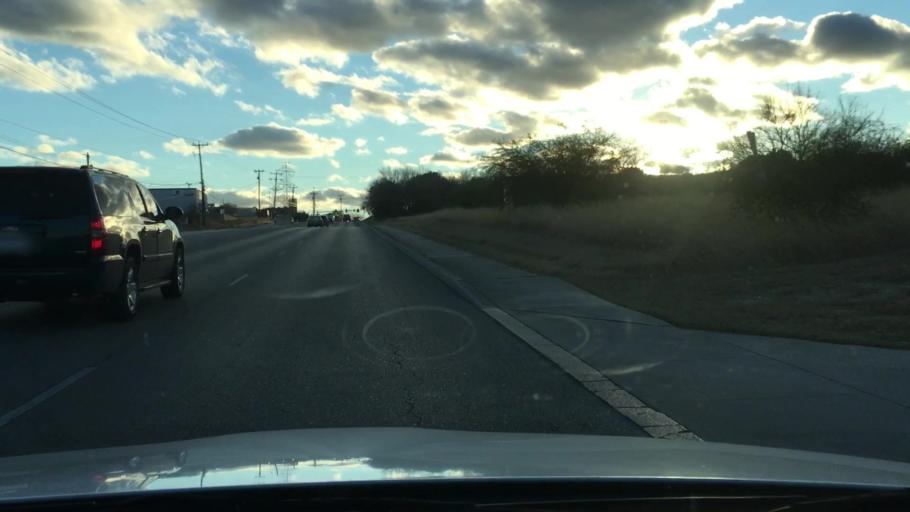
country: US
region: Texas
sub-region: Bexar County
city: Converse
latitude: 29.5253
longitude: -98.3428
